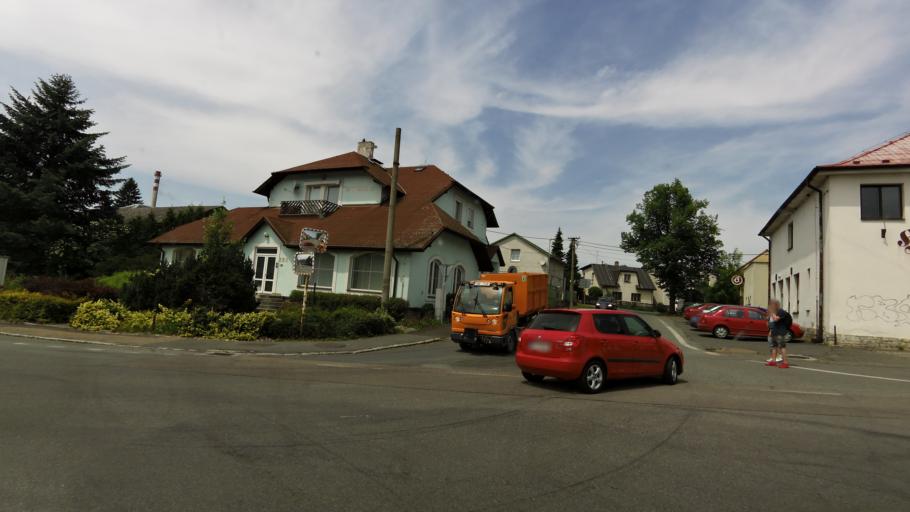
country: CZ
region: Plzensky
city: Holoubkov
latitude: 49.7758
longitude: 13.6924
